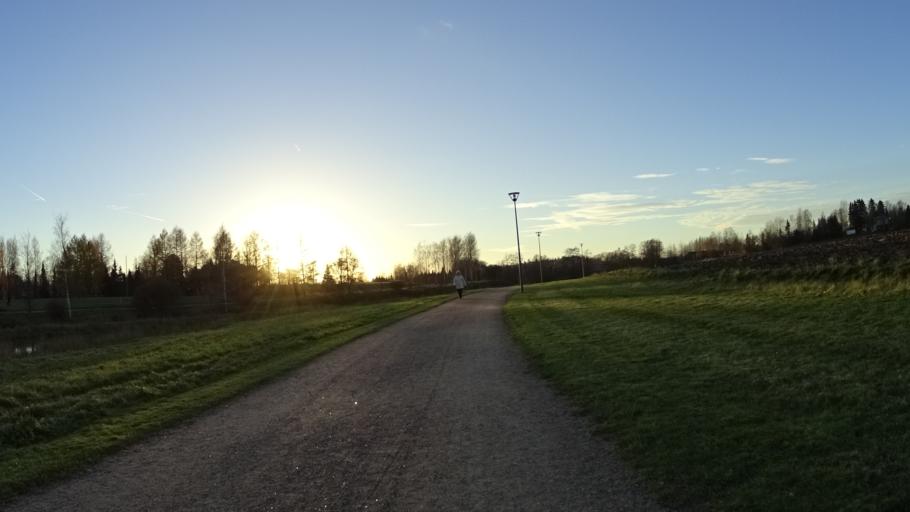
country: FI
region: Uusimaa
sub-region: Helsinki
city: Vantaa
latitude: 60.2803
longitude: 24.9903
